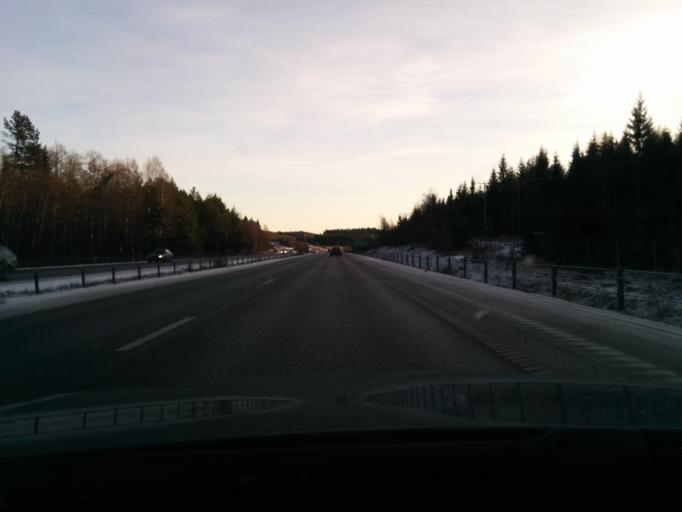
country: SE
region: Uppsala
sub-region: Habo Kommun
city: Balsta
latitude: 59.5594
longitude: 17.5751
